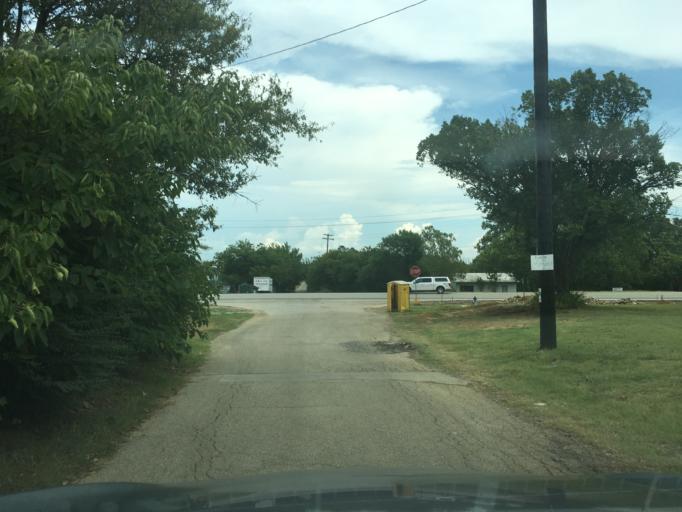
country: US
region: Texas
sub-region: Denton County
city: Denton
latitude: 33.1811
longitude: -97.1400
